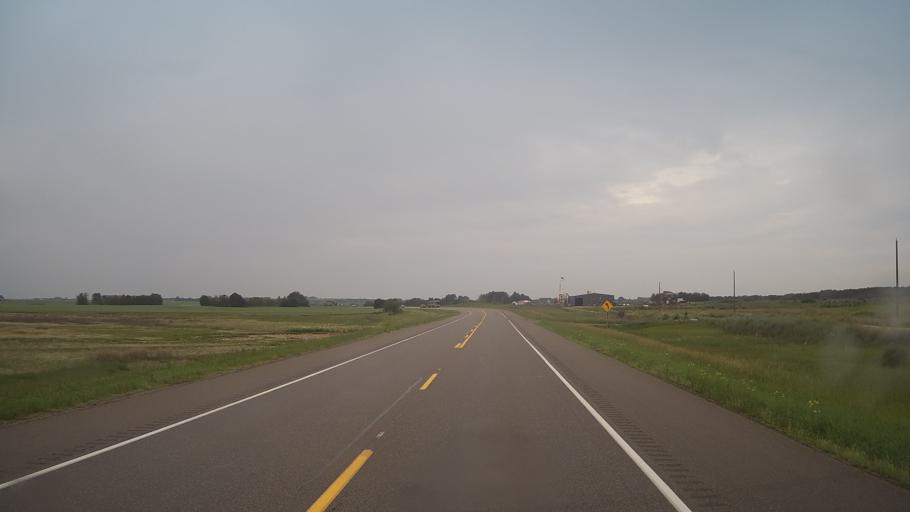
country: CA
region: Saskatchewan
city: Dalmeny
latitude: 52.1292
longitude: -106.8930
